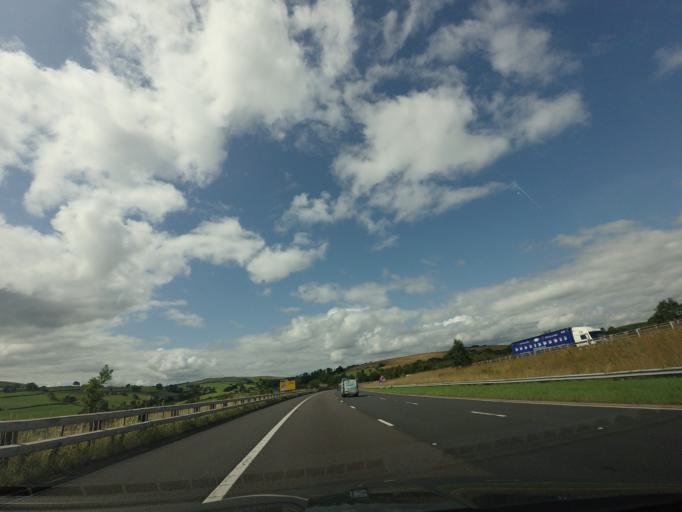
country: GB
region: England
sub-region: Cumbria
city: Sedbergh
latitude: 54.3660
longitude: -2.5909
